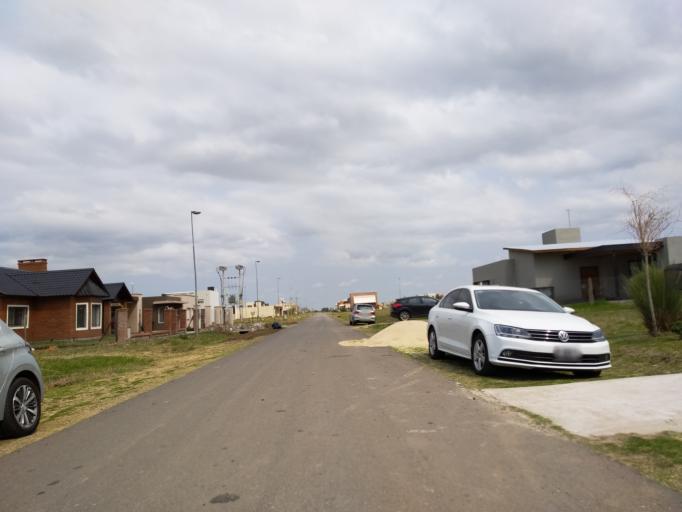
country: AR
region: Santa Fe
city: Funes
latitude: -32.9256
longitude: -60.8510
